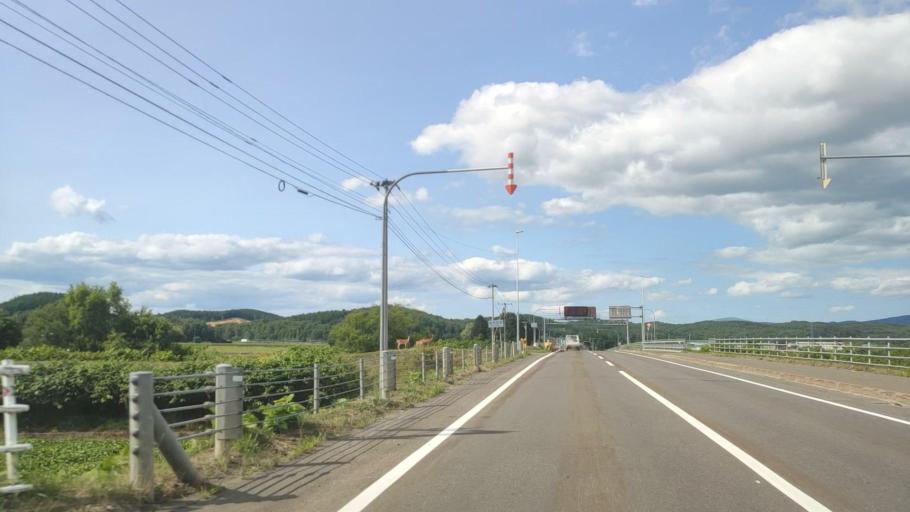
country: JP
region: Hokkaido
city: Nayoro
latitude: 44.3716
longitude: 142.4361
